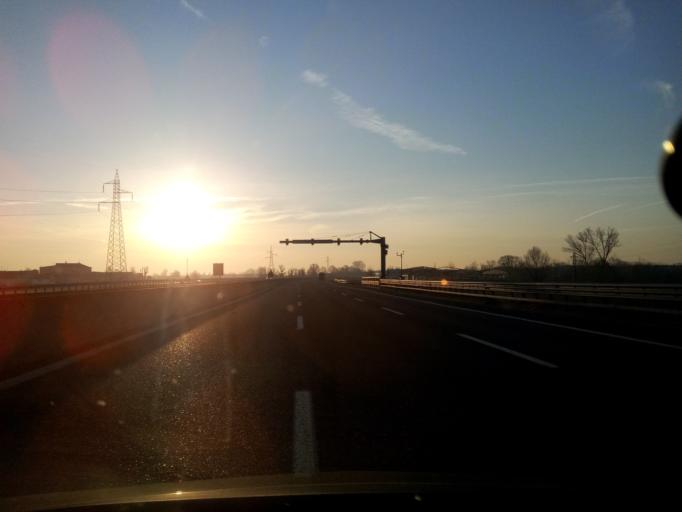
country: IT
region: Lombardy
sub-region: Citta metropolitana di Milano
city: Cerro al Lambro
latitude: 45.3358
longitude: 9.3465
